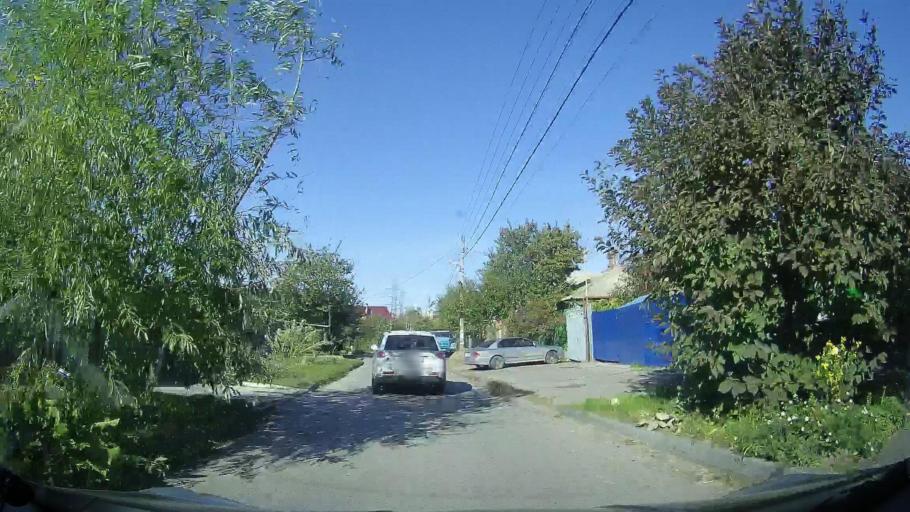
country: RU
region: Rostov
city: Rostov-na-Donu
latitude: 47.2368
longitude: 39.6734
